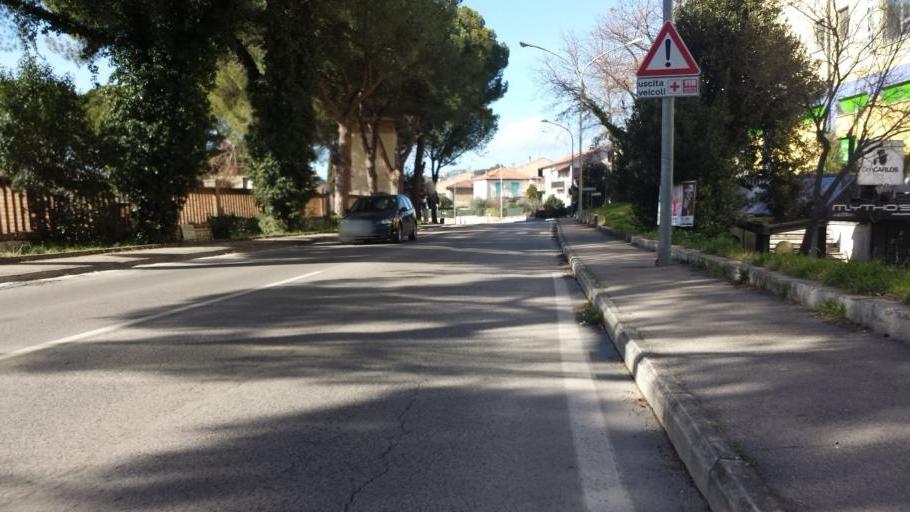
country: IT
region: Umbria
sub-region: Provincia di Terni
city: Terni
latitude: 42.5893
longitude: 12.6017
